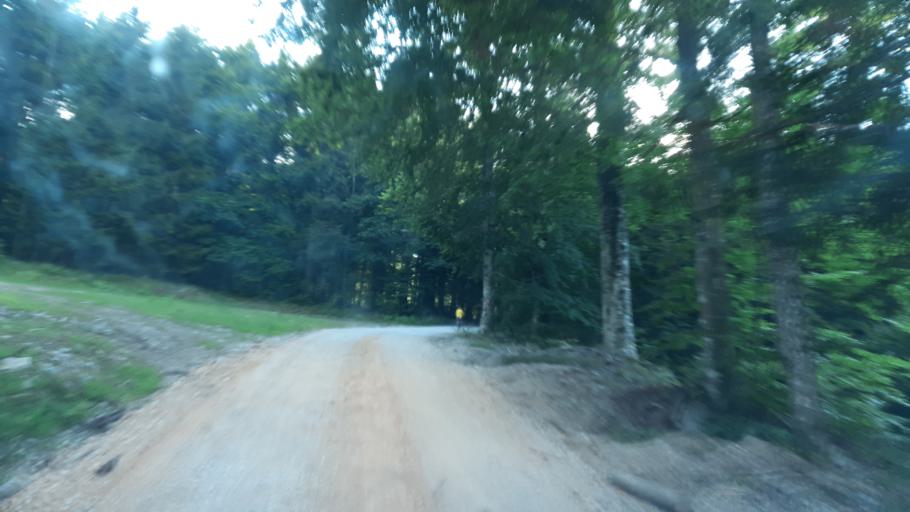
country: SI
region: Dolenjske Toplice
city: Dolenjske Toplice
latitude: 45.6923
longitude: 15.0080
